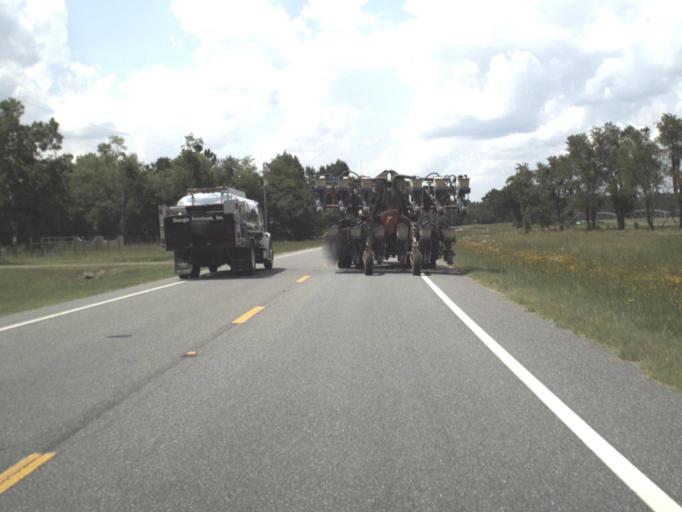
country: US
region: Georgia
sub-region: Echols County
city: Statenville
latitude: 30.5889
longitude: -83.0929
